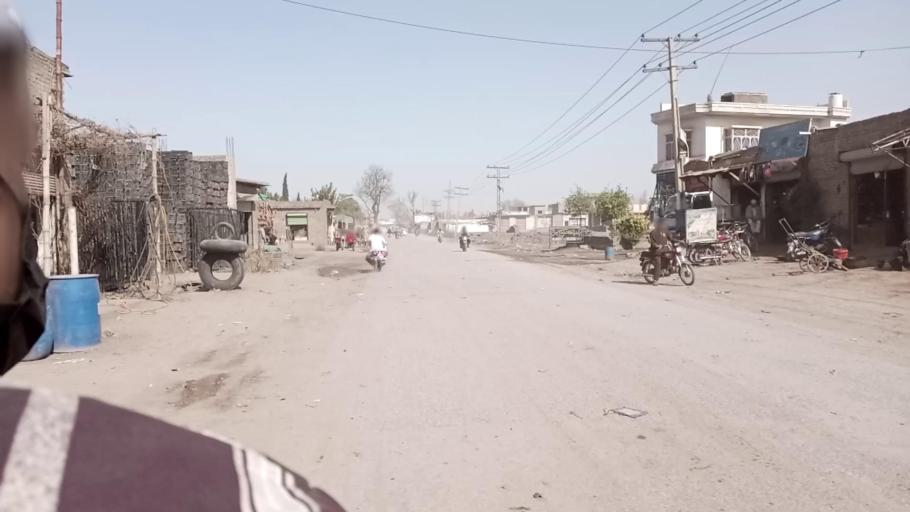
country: PK
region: Khyber Pakhtunkhwa
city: Peshawar
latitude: 33.9945
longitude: 71.6338
